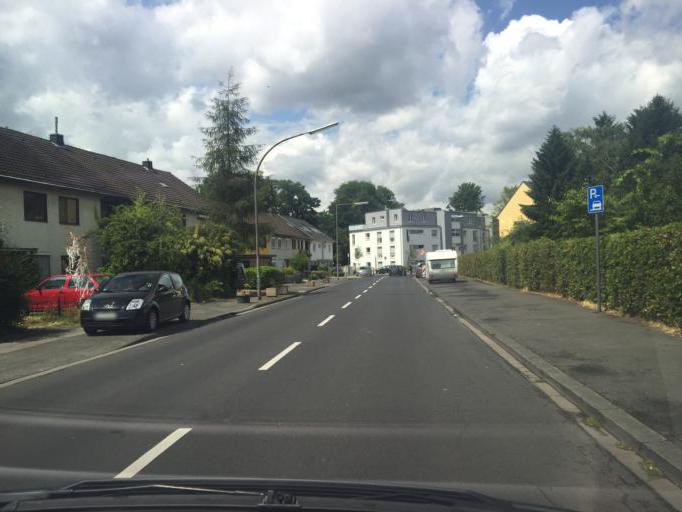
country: DE
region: North Rhine-Westphalia
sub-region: Regierungsbezirk Koln
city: Neustadt/Nord
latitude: 50.9557
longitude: 6.9445
